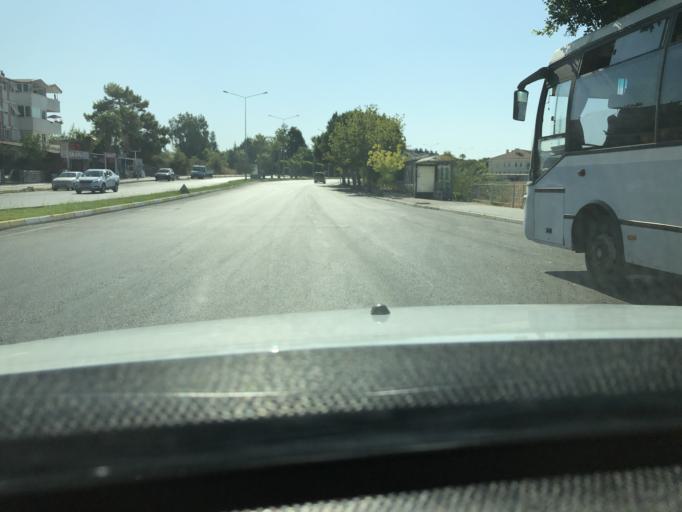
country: TR
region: Antalya
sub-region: Manavgat
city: Side
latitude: 36.7816
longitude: 31.3918
